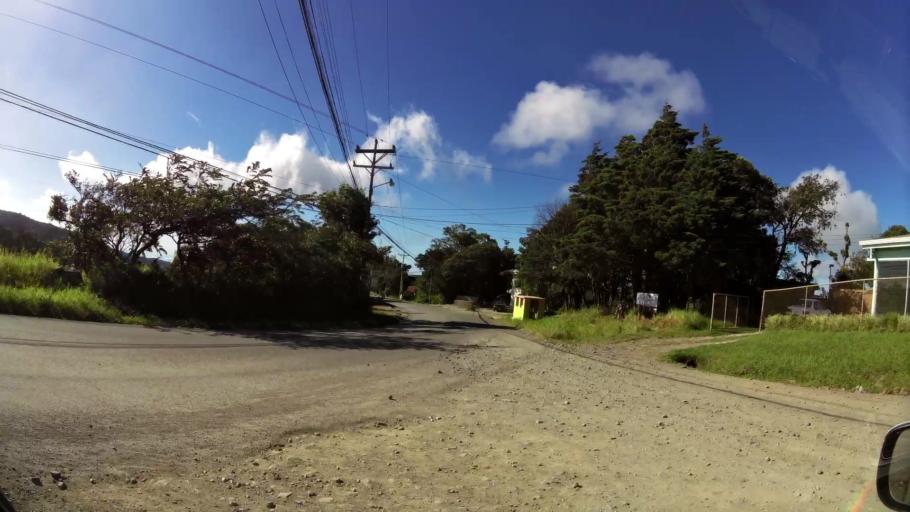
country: CR
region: Guanacaste
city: Juntas
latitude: 10.3144
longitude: -84.8274
